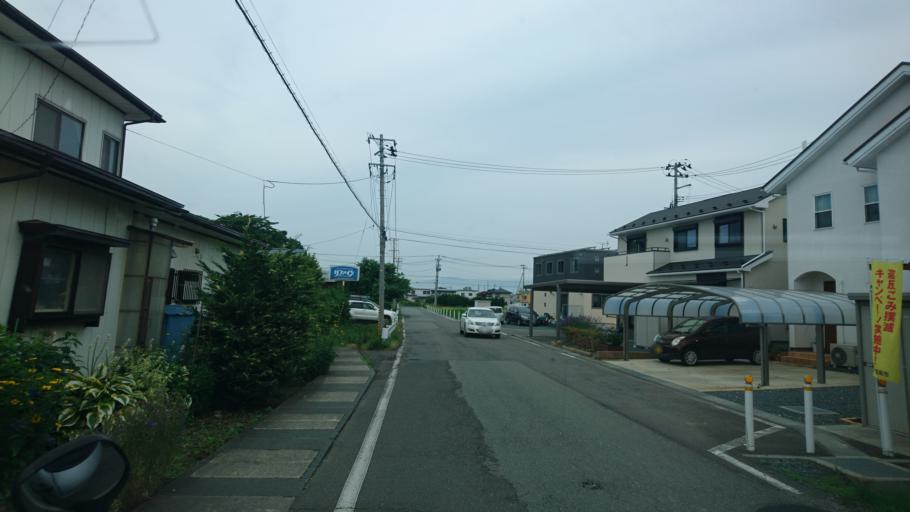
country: JP
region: Iwate
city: Morioka-shi
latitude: 39.6679
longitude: 141.1439
